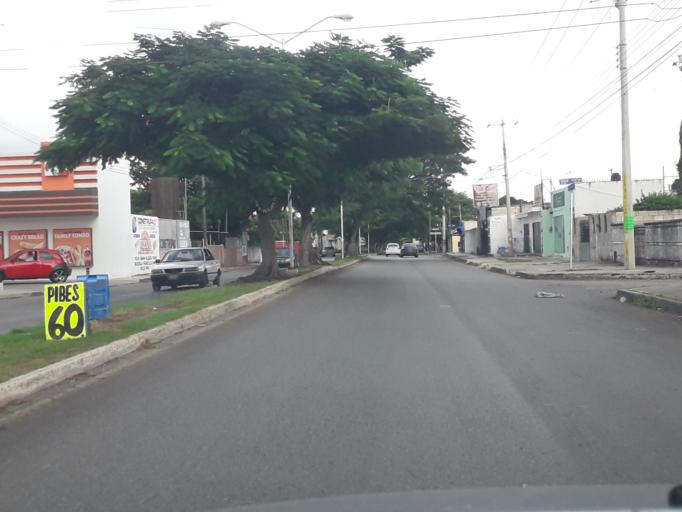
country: MX
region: Yucatan
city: Merida
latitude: 20.9622
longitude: -89.6586
